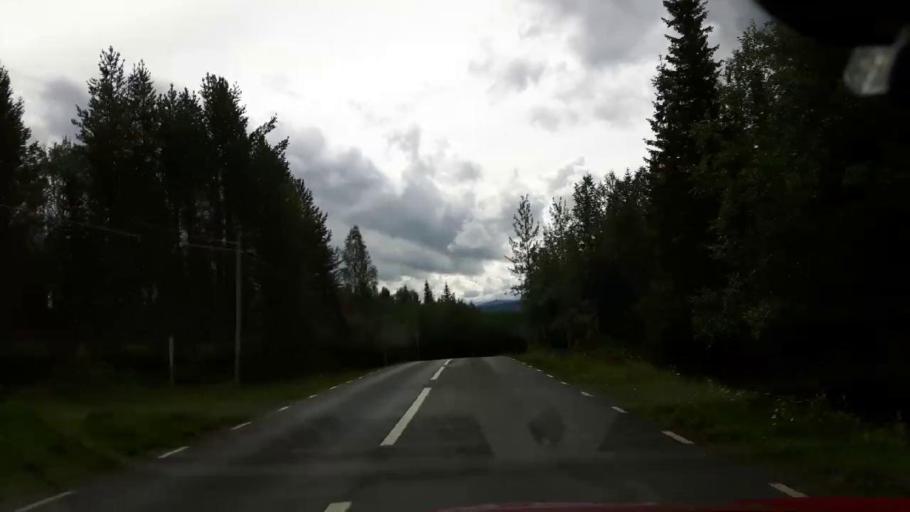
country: NO
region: Nord-Trondelag
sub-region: Lierne
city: Sandvika
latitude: 64.5192
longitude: 14.1623
